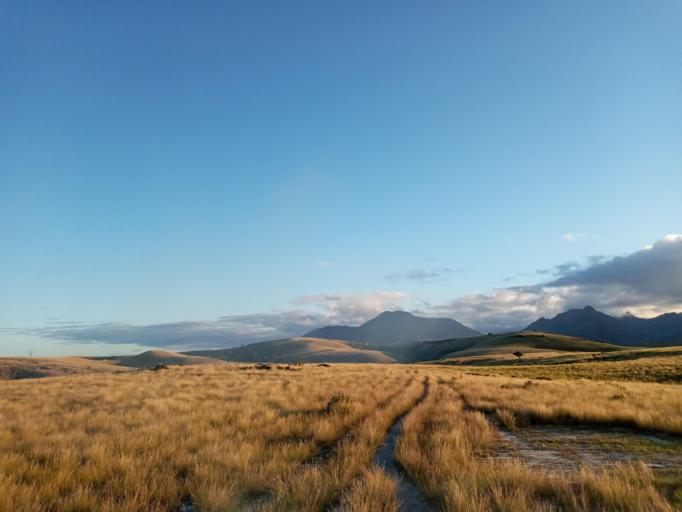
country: MG
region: Anosy
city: Fort Dauphin
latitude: -24.5113
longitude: 47.2567
